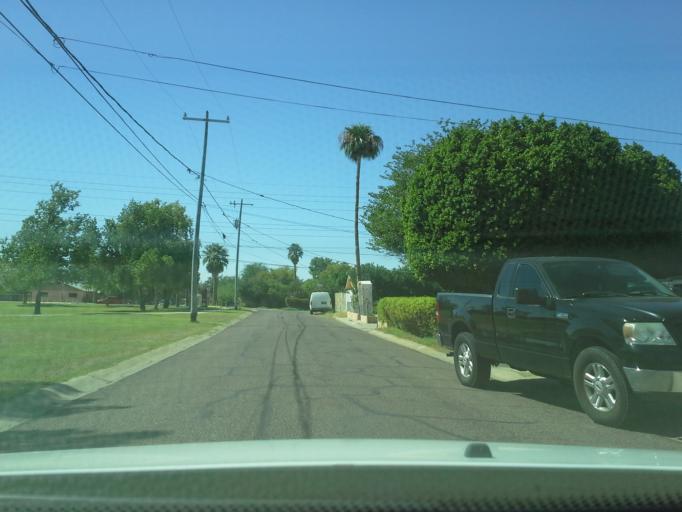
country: US
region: Arizona
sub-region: Maricopa County
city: Paradise Valley
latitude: 33.5723
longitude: -112.0557
